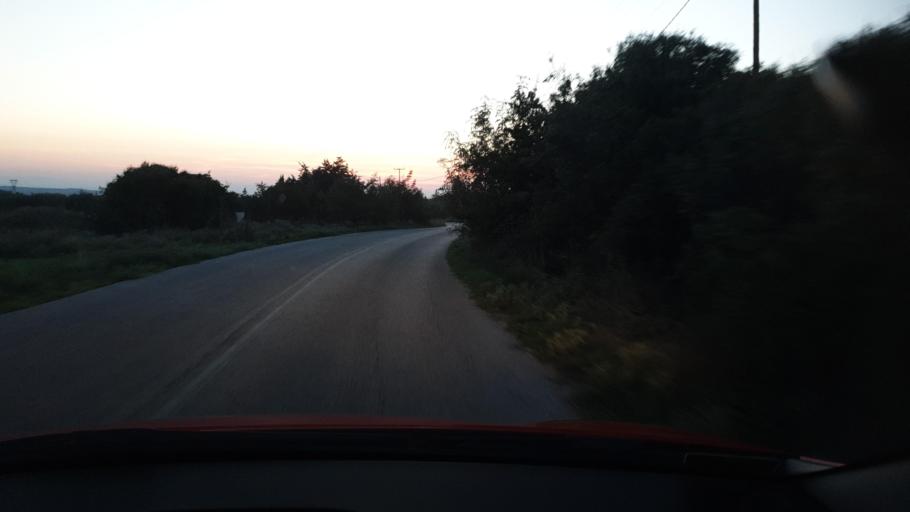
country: GR
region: Central Macedonia
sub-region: Nomos Thessalonikis
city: Vasilika
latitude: 40.5091
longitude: 23.1403
